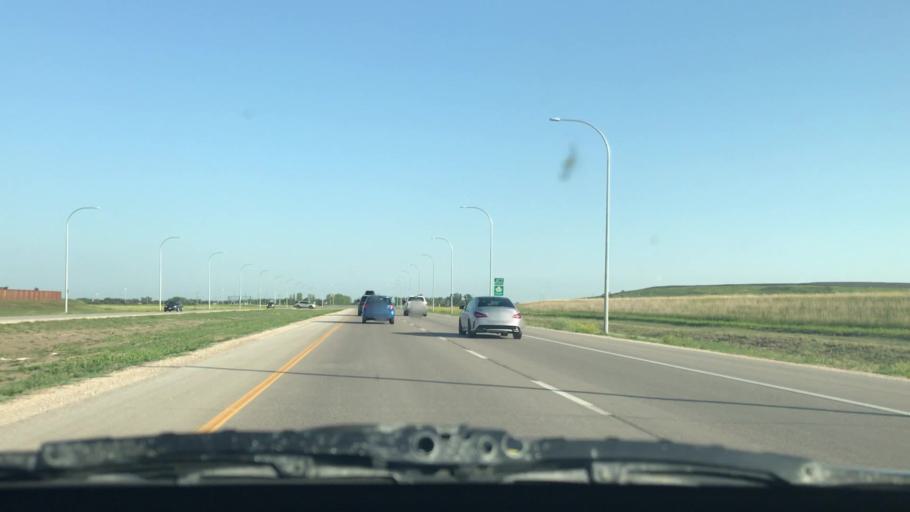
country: CA
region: Manitoba
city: Winnipeg
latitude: 49.7741
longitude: -97.1861
